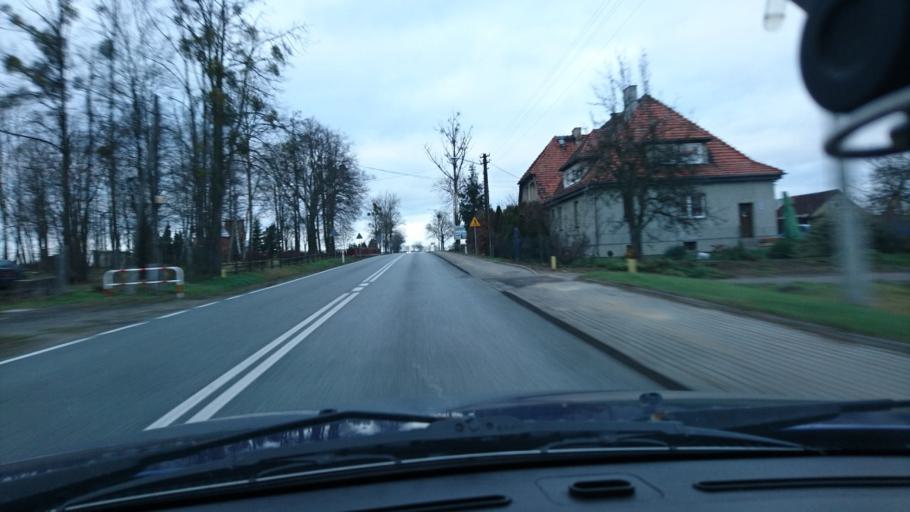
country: PL
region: Opole Voivodeship
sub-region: Powiat kluczborski
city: Byczyna
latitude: 51.0643
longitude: 18.2012
